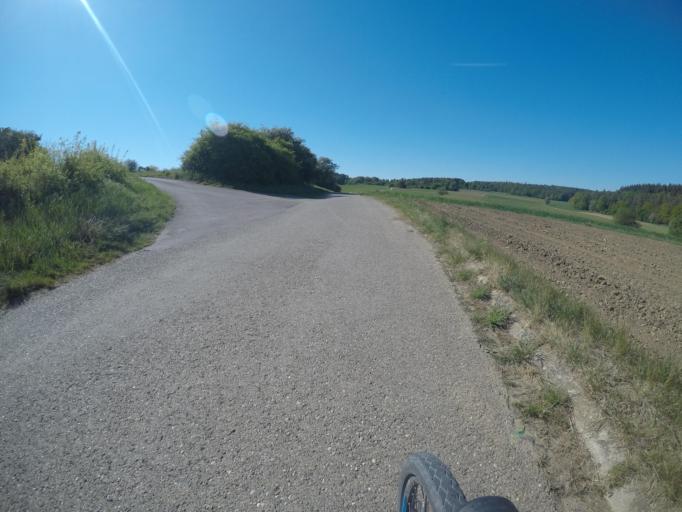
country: DE
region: Baden-Wuerttemberg
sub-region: Karlsruhe Region
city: Heimsheim
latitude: 48.8180
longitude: 8.8573
